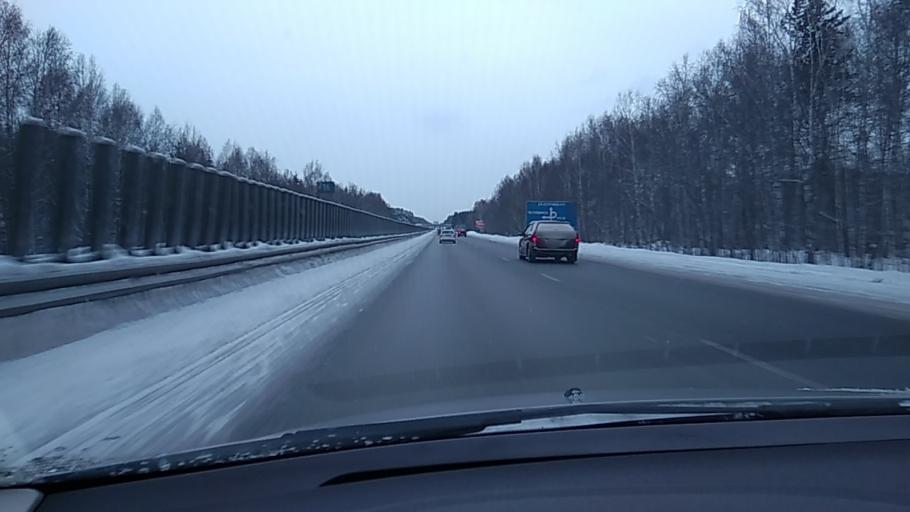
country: RU
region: Sverdlovsk
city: Istok
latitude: 56.7999
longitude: 60.8052
